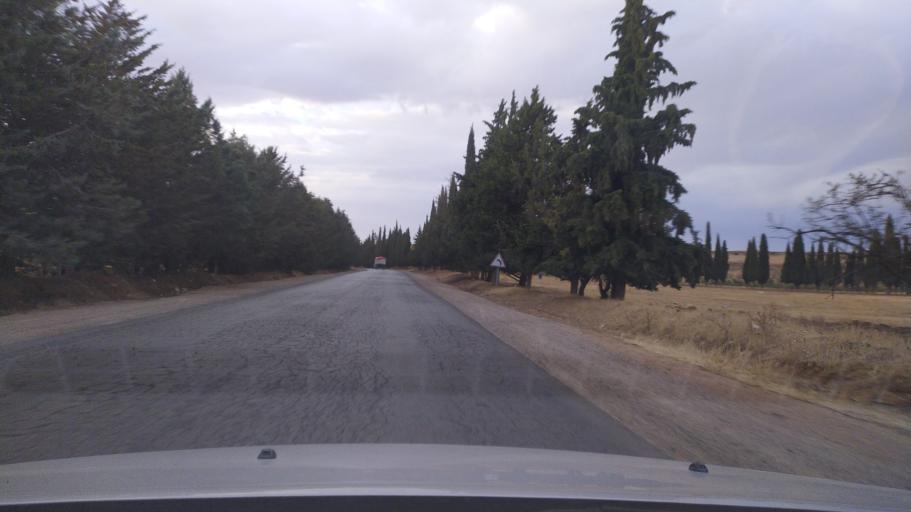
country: DZ
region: Tiaret
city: Frenda
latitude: 35.0444
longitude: 1.0861
